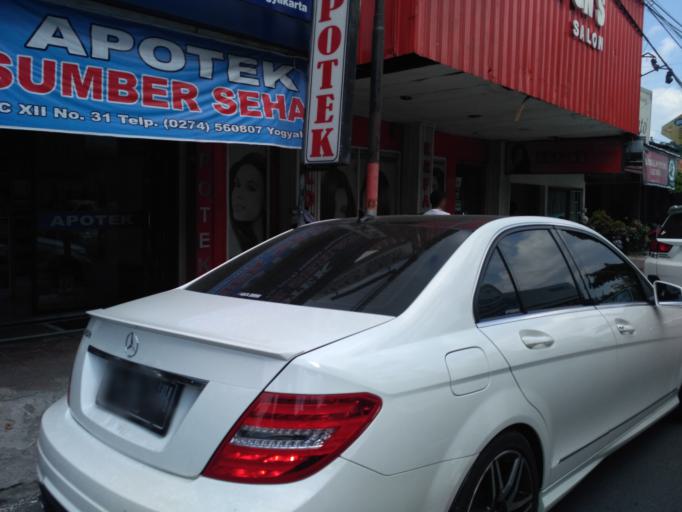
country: ID
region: Daerah Istimewa Yogyakarta
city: Depok
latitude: -7.7607
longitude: 110.3947
